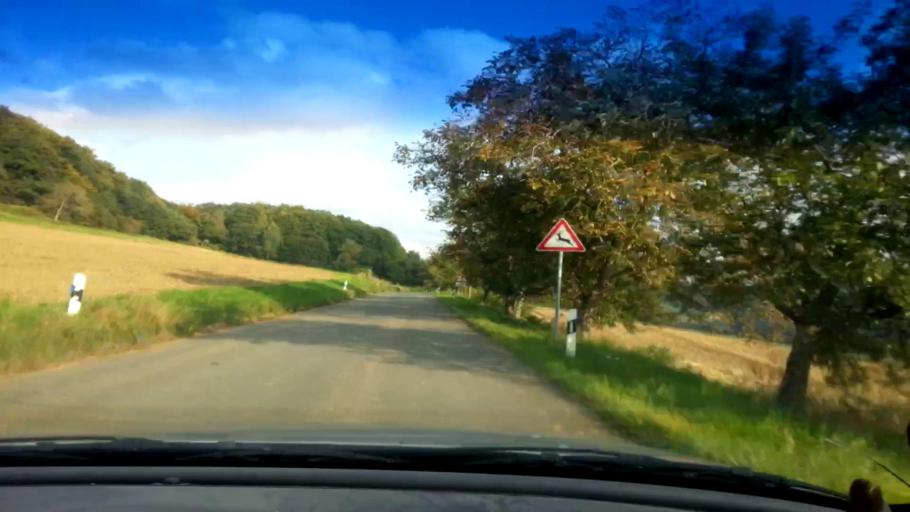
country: DE
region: Bavaria
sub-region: Upper Franconia
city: Schesslitz
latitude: 50.0095
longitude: 11.0516
